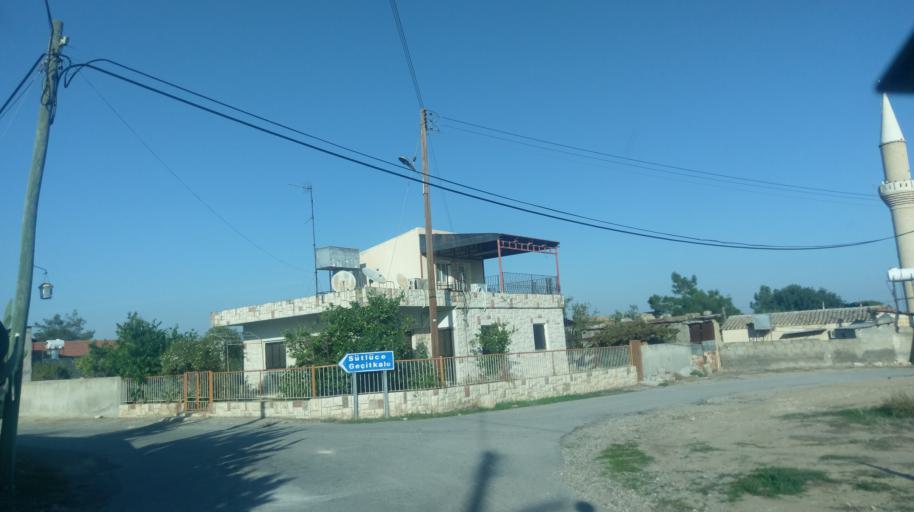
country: CY
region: Ammochostos
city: Lefkonoiko
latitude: 35.2171
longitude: 33.6987
